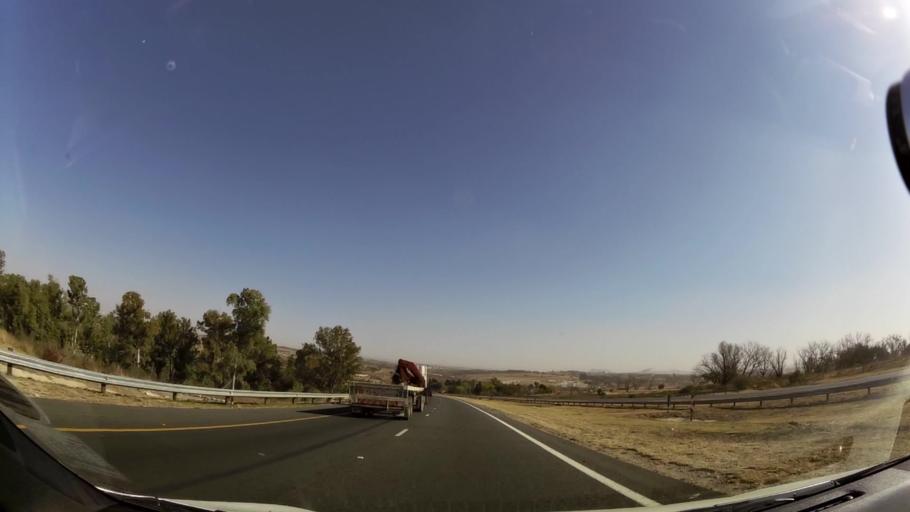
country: ZA
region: Gauteng
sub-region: City of Johannesburg Metropolitan Municipality
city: Diepsloot
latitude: -25.9429
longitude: 27.9628
